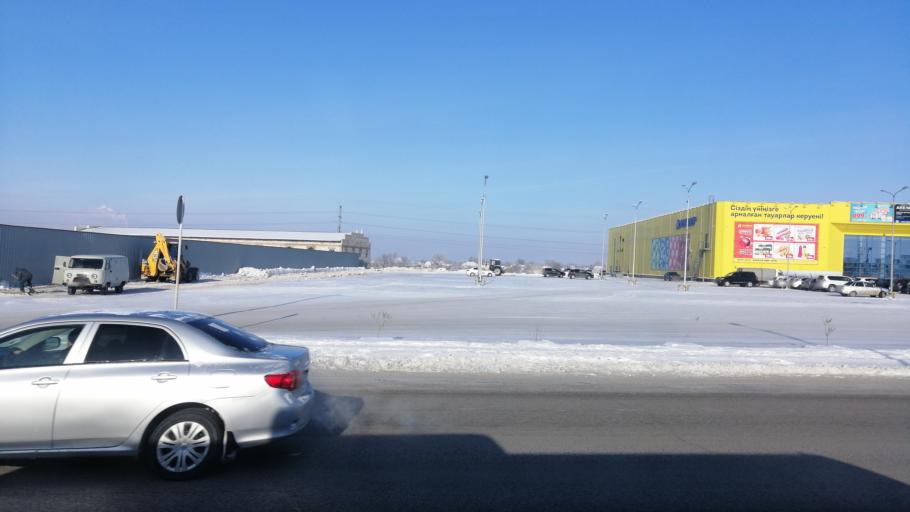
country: KZ
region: Aqtoebe
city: Aqtobe
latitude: 50.2982
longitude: 57.1905
